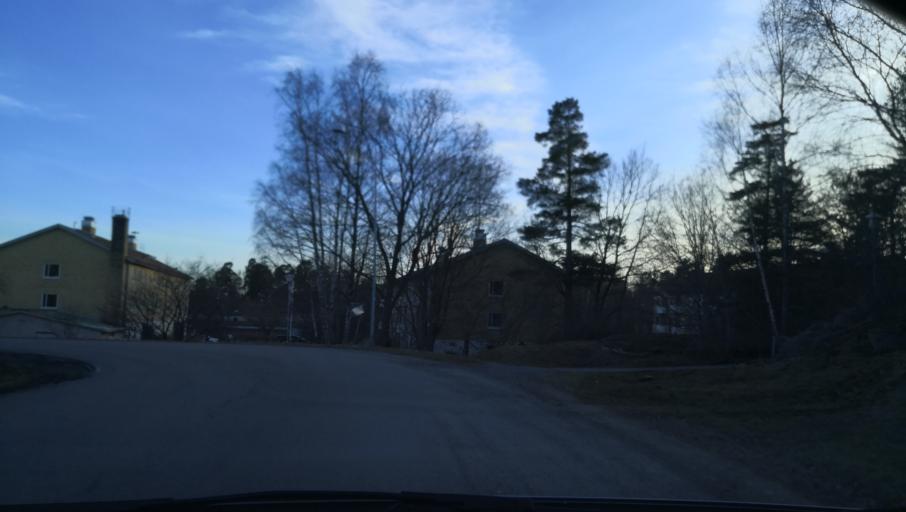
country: SE
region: Stockholm
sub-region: Varmdo Kommun
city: Gustavsberg
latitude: 59.3377
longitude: 18.3931
